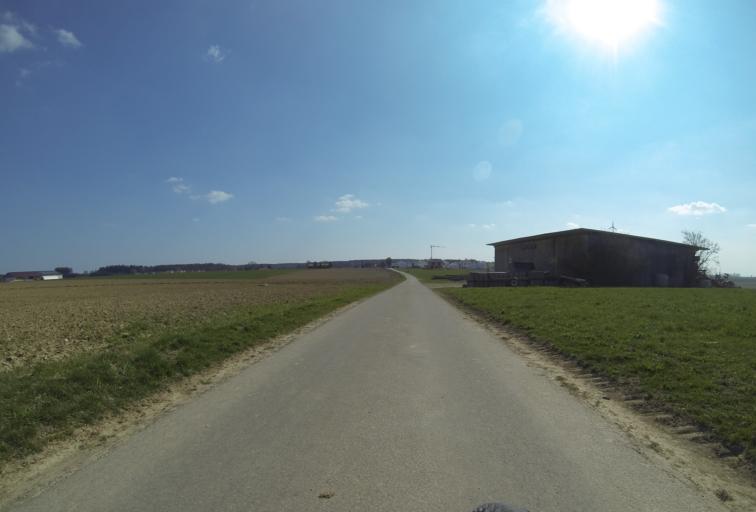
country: DE
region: Baden-Wuerttemberg
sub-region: Tuebingen Region
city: Huttisheim
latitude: 48.2677
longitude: 9.9578
